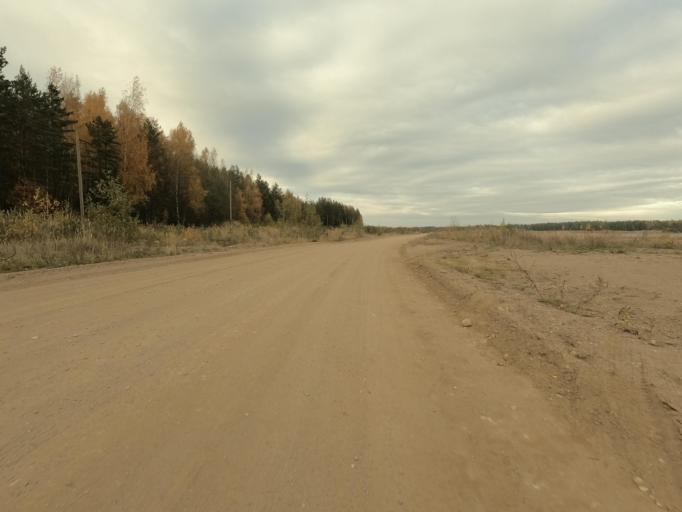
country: RU
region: Leningrad
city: Priladozhskiy
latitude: 59.7019
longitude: 31.3626
